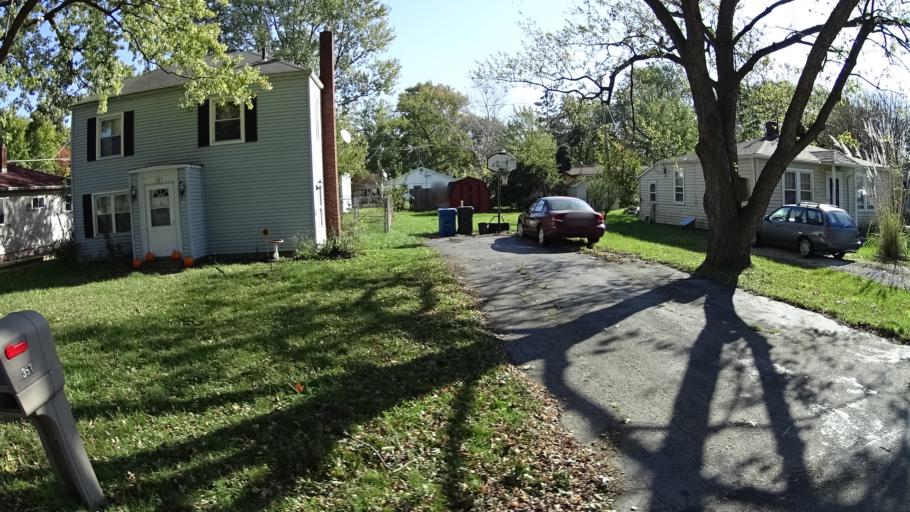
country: US
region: Ohio
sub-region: Lorain County
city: Vermilion-on-the-Lake
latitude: 41.4271
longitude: -82.3414
